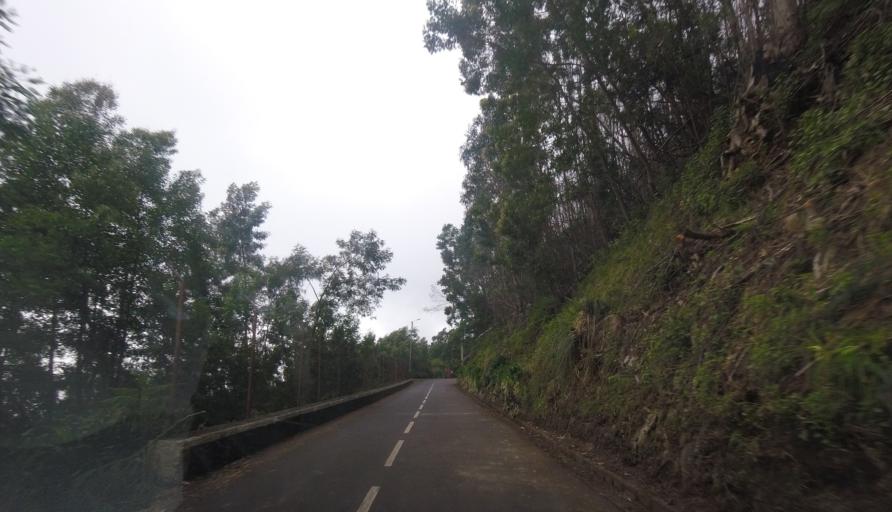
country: PT
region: Madeira
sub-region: Funchal
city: Nossa Senhora do Monte
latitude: 32.6902
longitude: -16.8909
